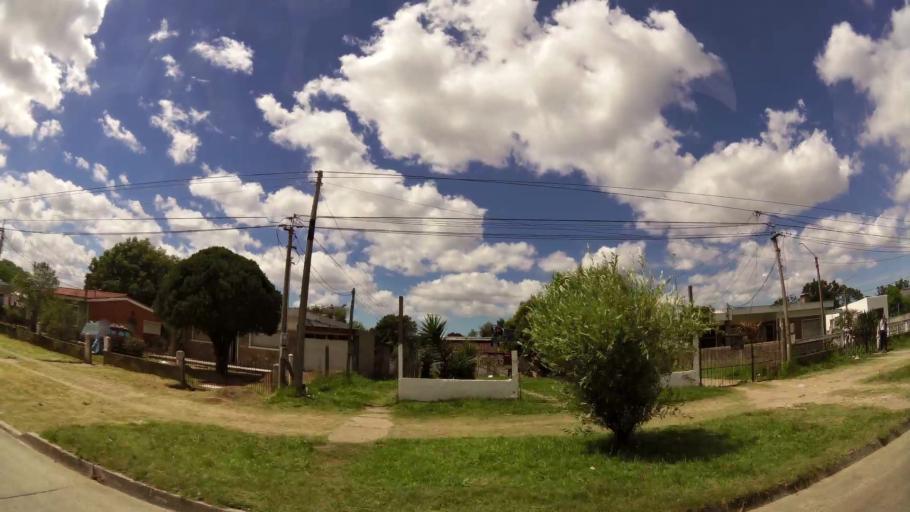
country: UY
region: Canelones
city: Colonia Nicolich
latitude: -34.8259
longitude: -56.1152
